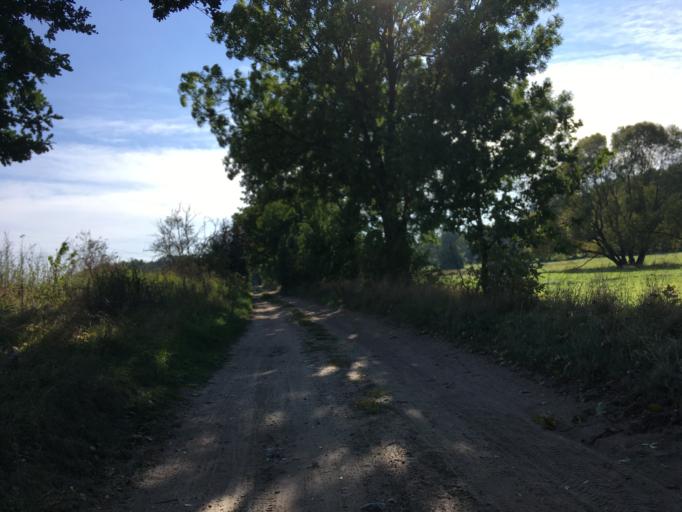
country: DE
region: Brandenburg
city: Altlandsberg
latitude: 52.5471
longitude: 13.7246
